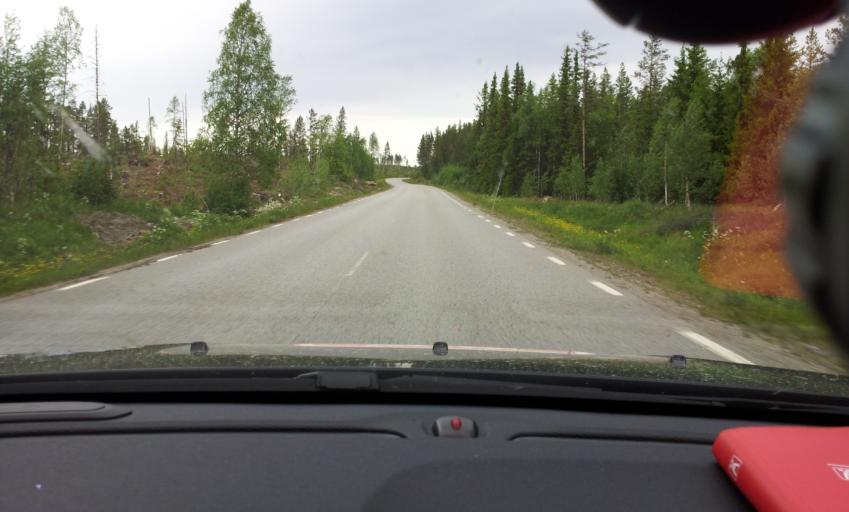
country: SE
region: Jaemtland
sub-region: Bergs Kommun
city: Hoverberg
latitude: 62.6869
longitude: 14.6358
